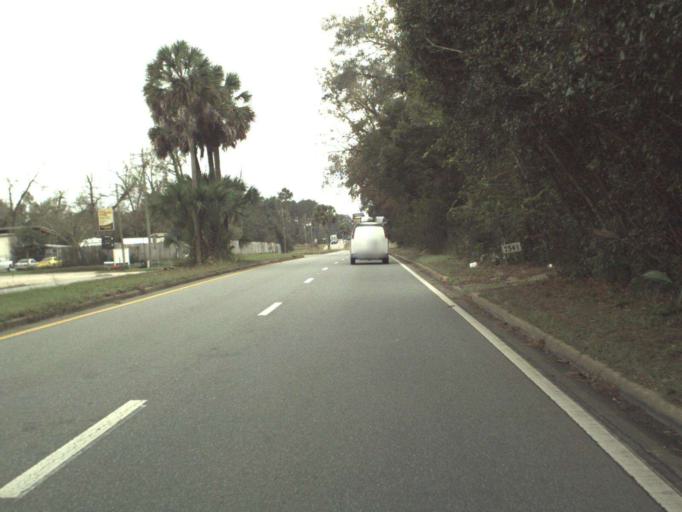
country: US
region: Florida
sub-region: Gadsden County
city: Havana
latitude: 30.6494
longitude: -84.4171
